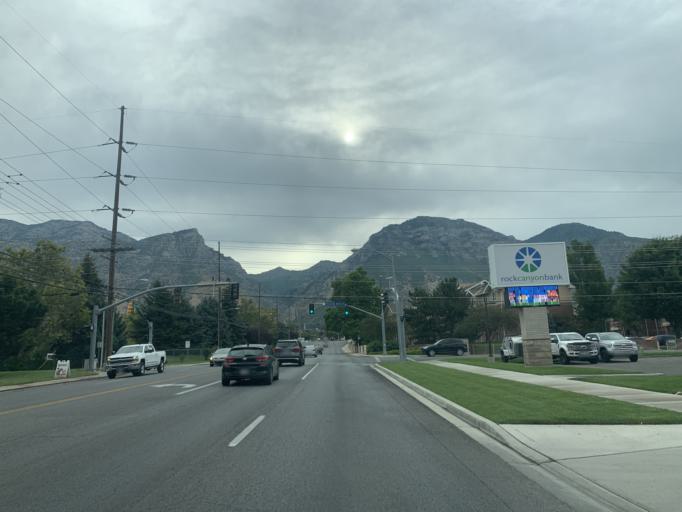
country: US
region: Utah
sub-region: Utah County
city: Provo
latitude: 40.2634
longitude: -111.6620
